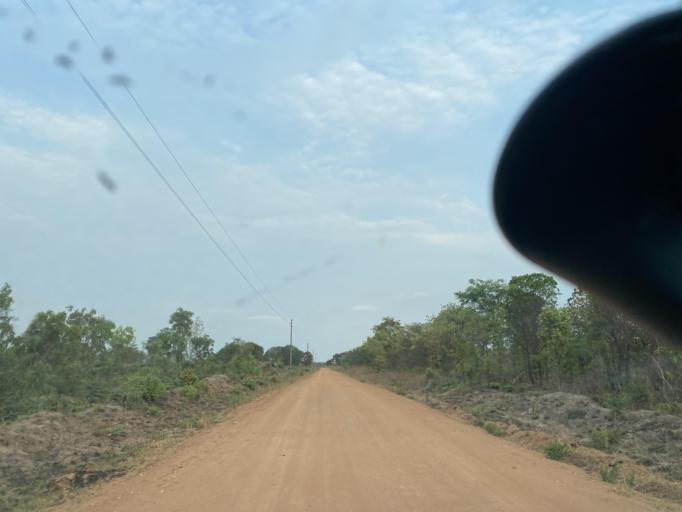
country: ZM
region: Lusaka
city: Chongwe
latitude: -15.1941
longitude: 28.5780
